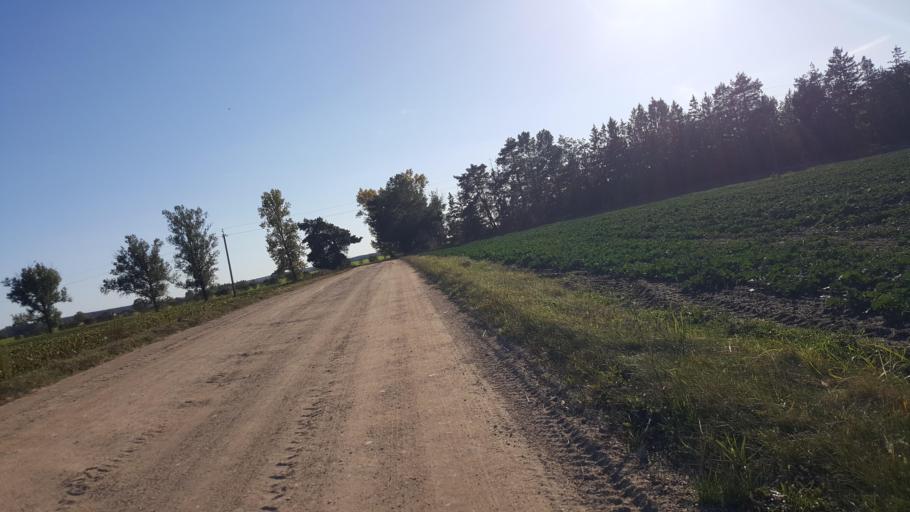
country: BY
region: Brest
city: Kamyanyets
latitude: 52.3759
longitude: 23.8782
